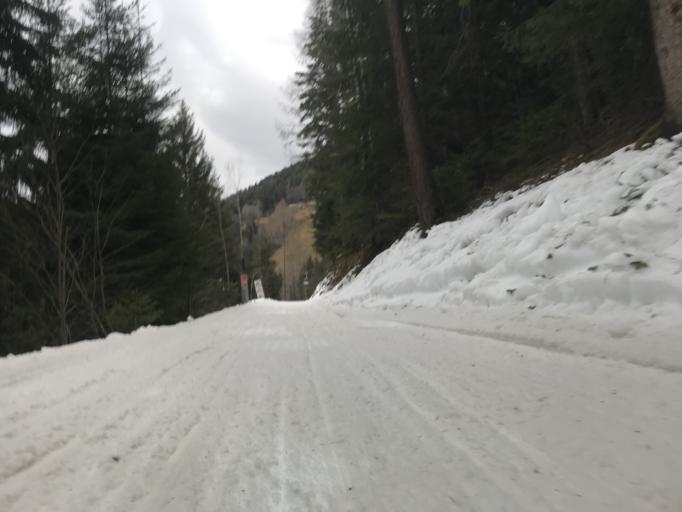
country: IT
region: Trentino-Alto Adige
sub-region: Bolzano
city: Bressanone
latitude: 46.6940
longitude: 11.6873
